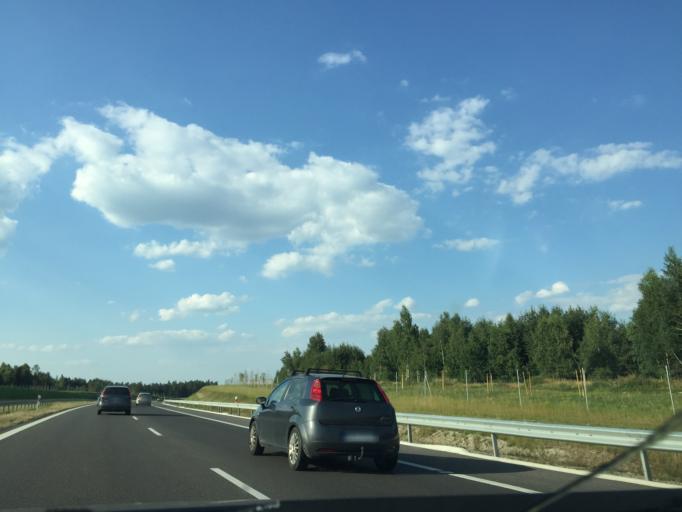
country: PL
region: Swietokrzyskie
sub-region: Powiat skarzyski
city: Skarzysko-Kamienna
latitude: 51.1379
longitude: 20.8325
